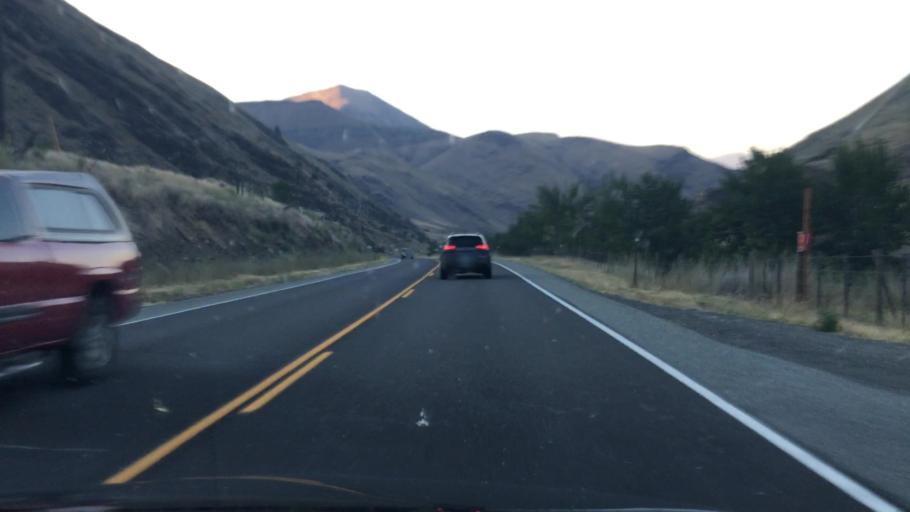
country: US
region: Idaho
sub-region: Valley County
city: McCall
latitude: 45.3802
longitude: -116.3515
